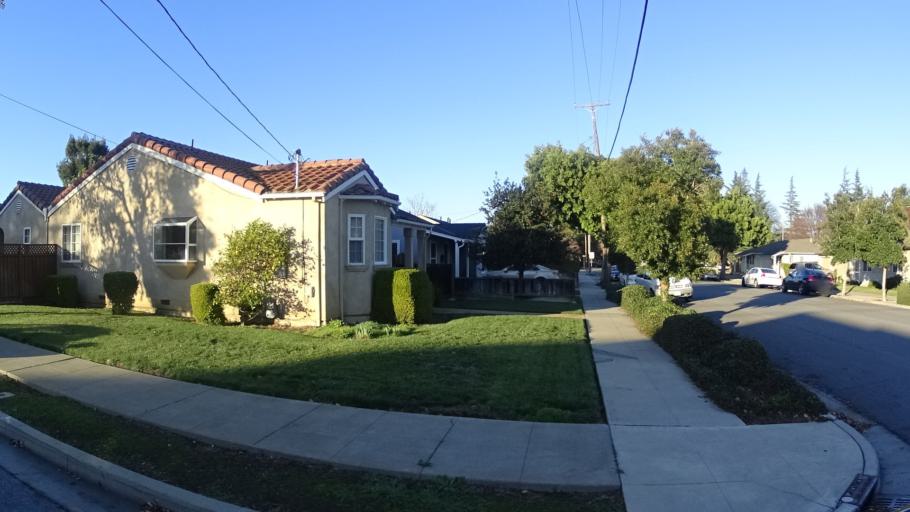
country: US
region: California
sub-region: Santa Clara County
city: Sunnyvale
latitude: 37.3734
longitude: -122.0242
